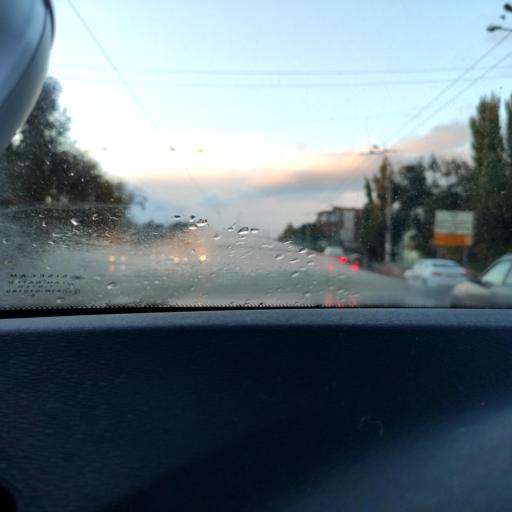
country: RU
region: Samara
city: Smyshlyayevka
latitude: 53.2061
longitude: 50.2789
